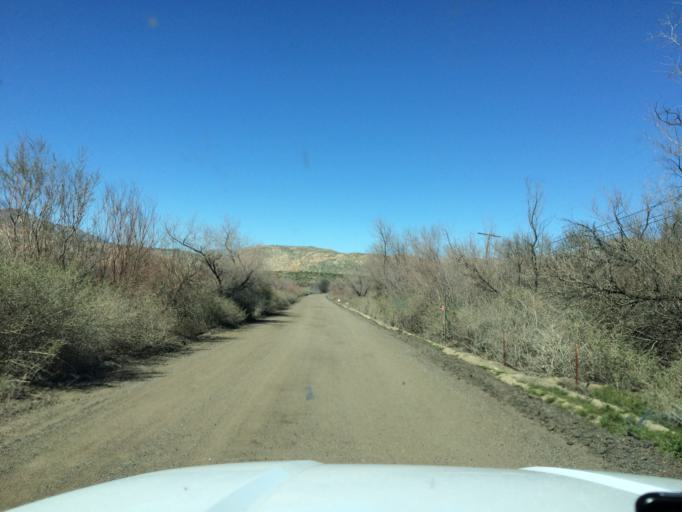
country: MX
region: Baja California
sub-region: Tecate
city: Cereso del Hongo
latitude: 32.6486
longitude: -116.1867
